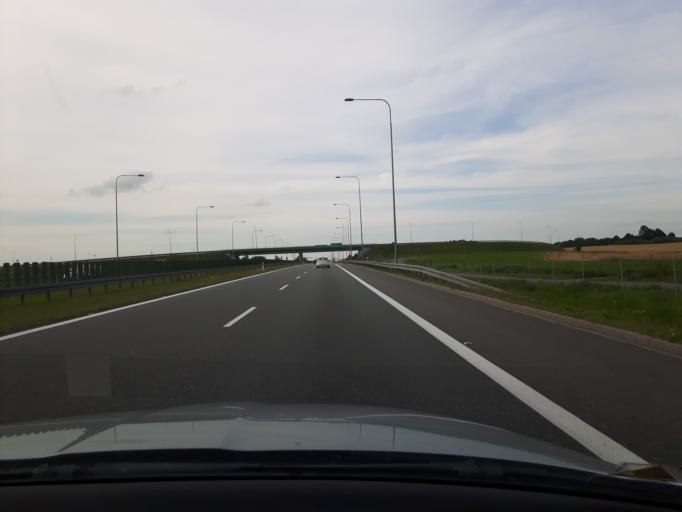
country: PL
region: Warmian-Masurian Voivodeship
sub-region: Powiat ostrodzki
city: Maldyty
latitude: 53.9662
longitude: 19.6982
